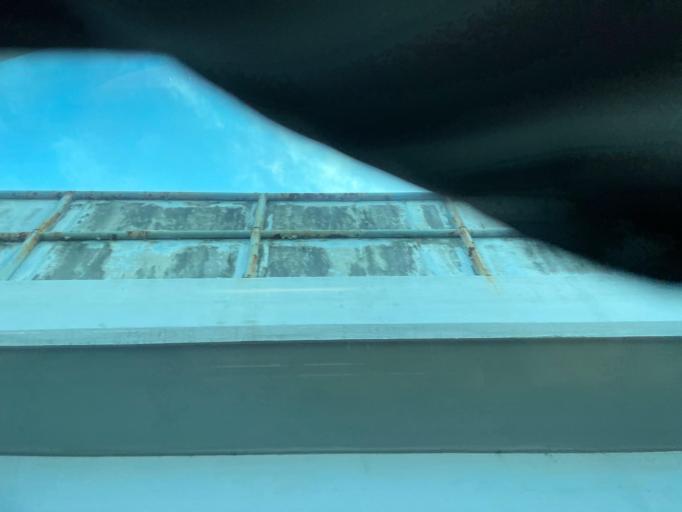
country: JP
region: Kanagawa
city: Kamakura
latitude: 35.3682
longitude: 139.5329
